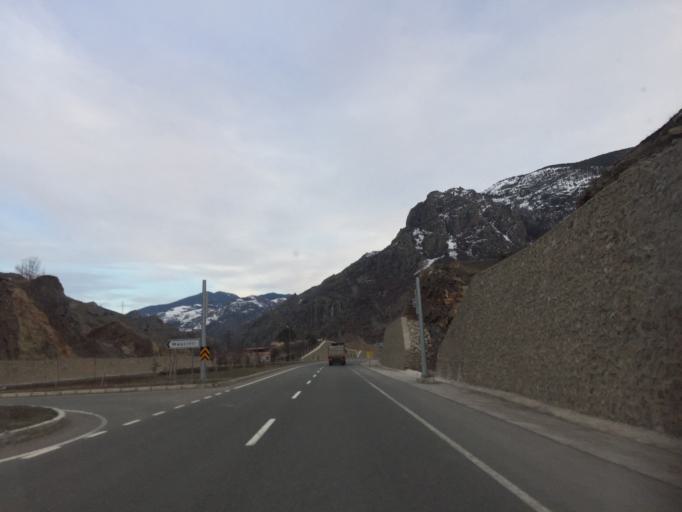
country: TR
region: Gumushane
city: Gumushkhane
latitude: 40.5035
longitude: 39.4268
